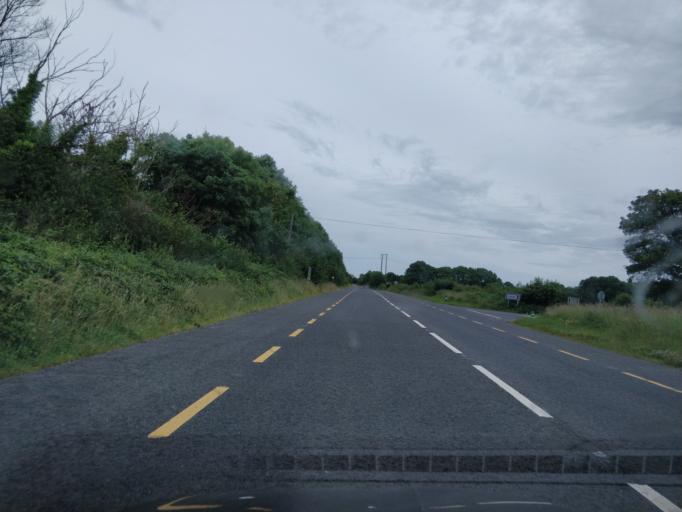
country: IE
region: Leinster
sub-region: Uibh Fhaili
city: Ferbane
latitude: 53.1674
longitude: -7.7707
